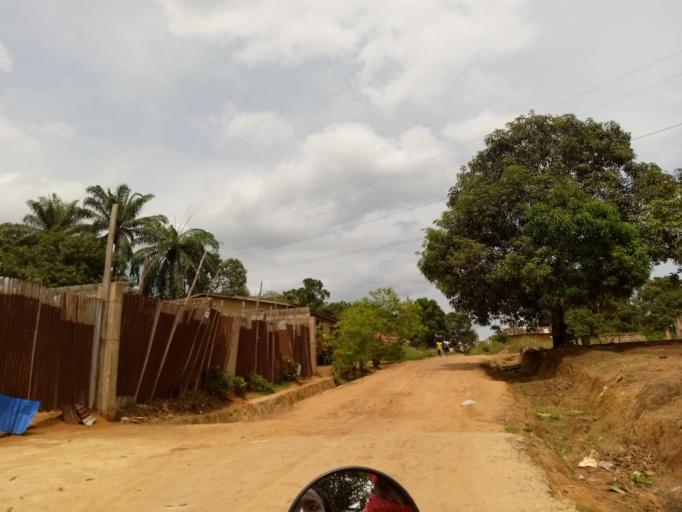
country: SL
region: Western Area
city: Waterloo
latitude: 8.3310
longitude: -13.0170
